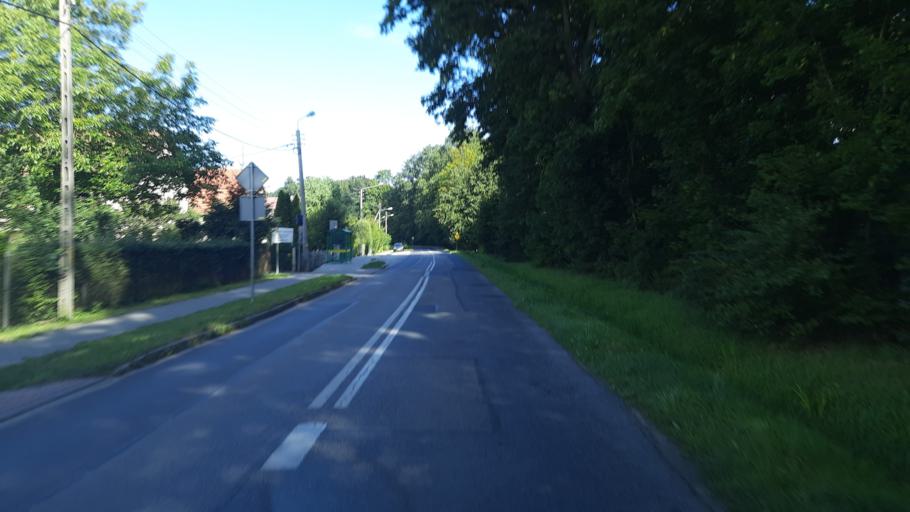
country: PL
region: Lower Silesian Voivodeship
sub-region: Powiat wroclawski
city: Dlugoleka
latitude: 51.1823
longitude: 17.1892
